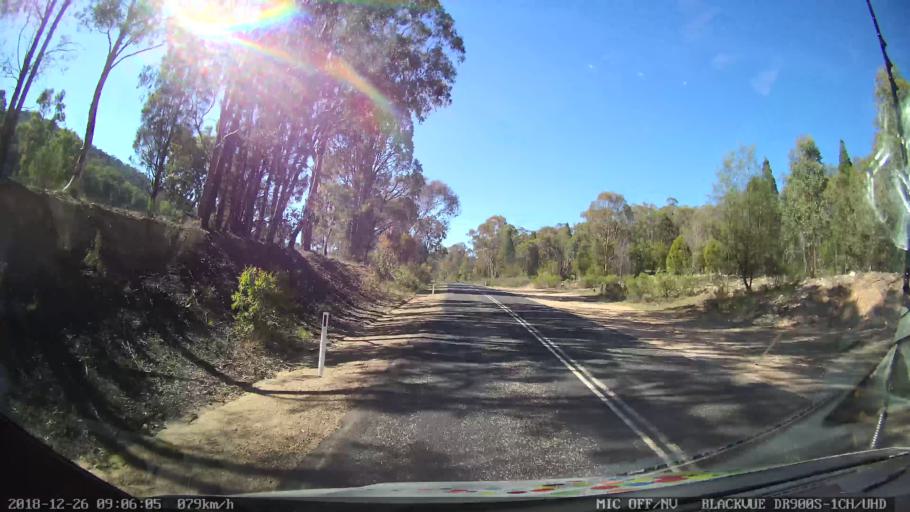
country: AU
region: New South Wales
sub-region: Mid-Western Regional
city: Kandos
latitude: -32.6899
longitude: 150.0045
